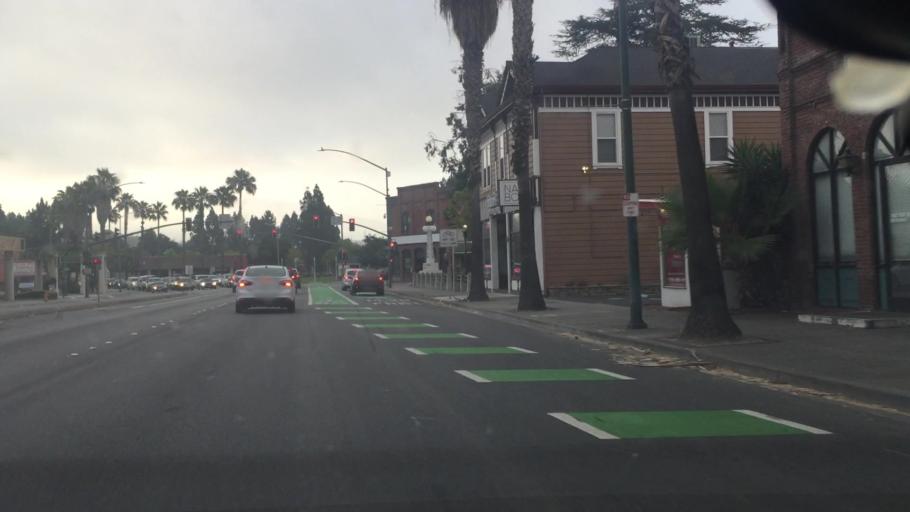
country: US
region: California
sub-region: Alameda County
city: Fremont
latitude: 37.5334
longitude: -121.9601
